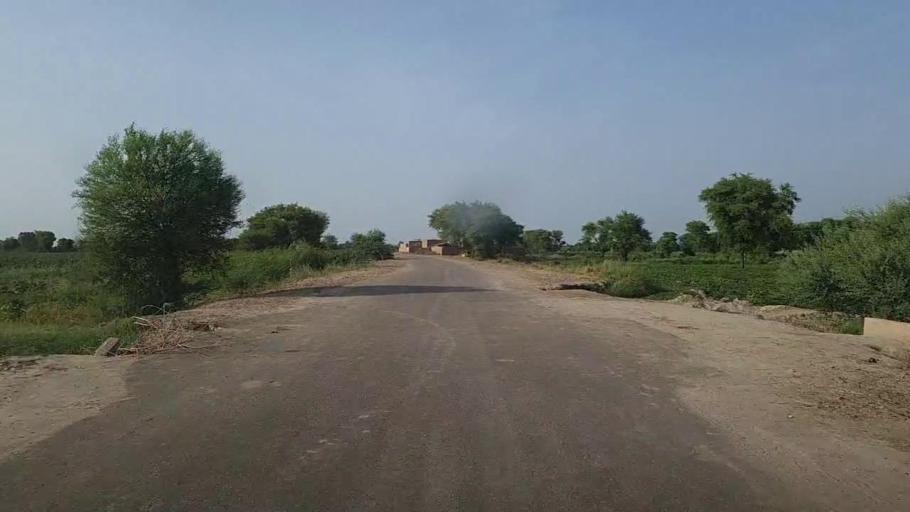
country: PK
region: Sindh
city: Ubauro
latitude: 28.0953
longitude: 69.8454
